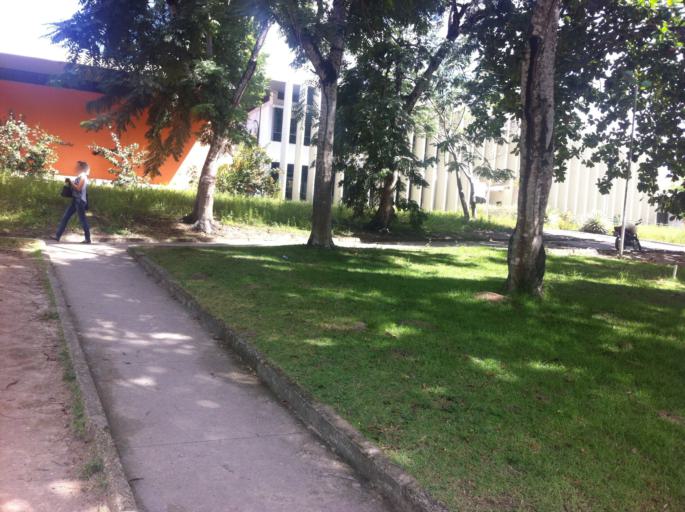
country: BR
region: Alagoas
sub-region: Satuba
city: Satuba
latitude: -9.5551
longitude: -35.7765
